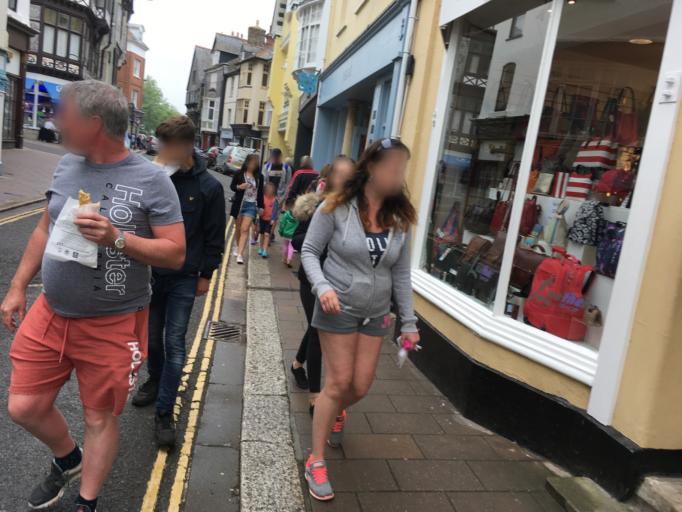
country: GB
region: England
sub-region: Devon
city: Dartmouth
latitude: 50.3505
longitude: -3.5783
